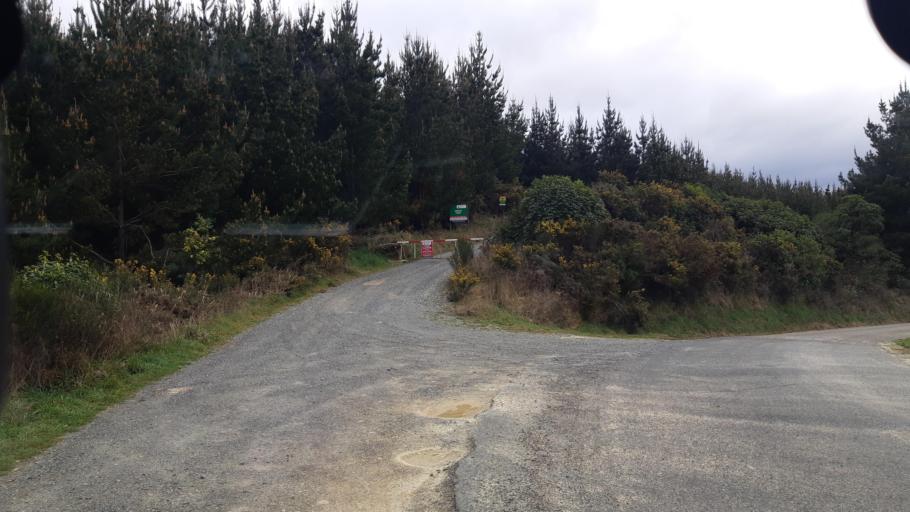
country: NZ
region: Tasman
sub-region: Tasman District
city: Motueka
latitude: -41.2638
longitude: 172.8856
